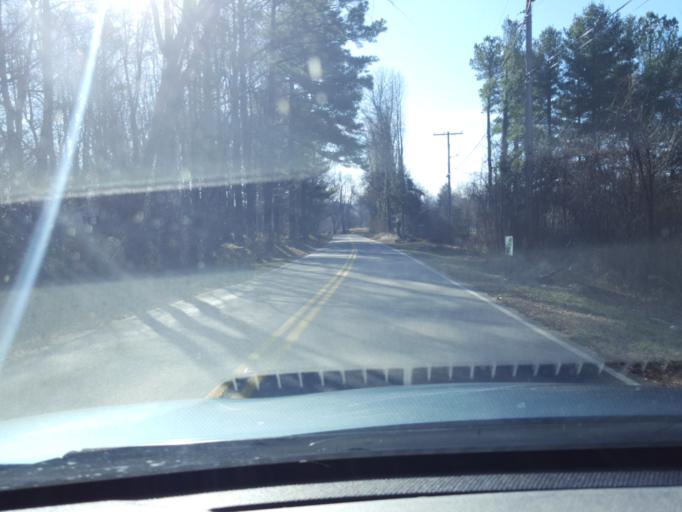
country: US
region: Maryland
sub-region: Calvert County
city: Chesapeake Beach
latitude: 38.6368
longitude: -76.5369
